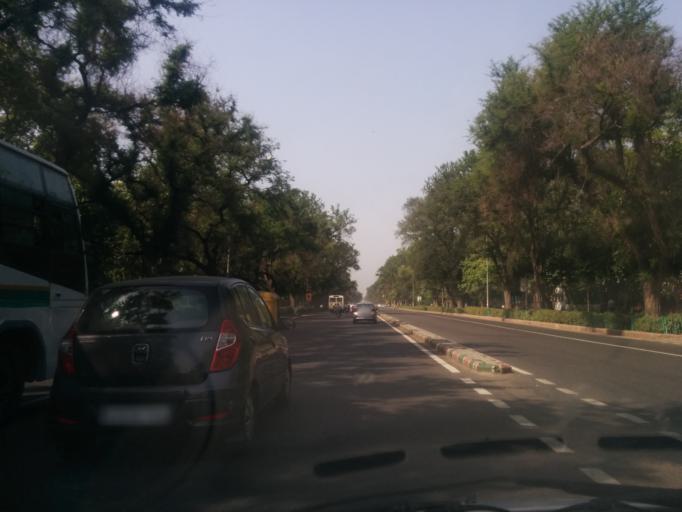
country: IN
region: NCT
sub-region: New Delhi
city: New Delhi
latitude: 28.6231
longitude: 77.2387
